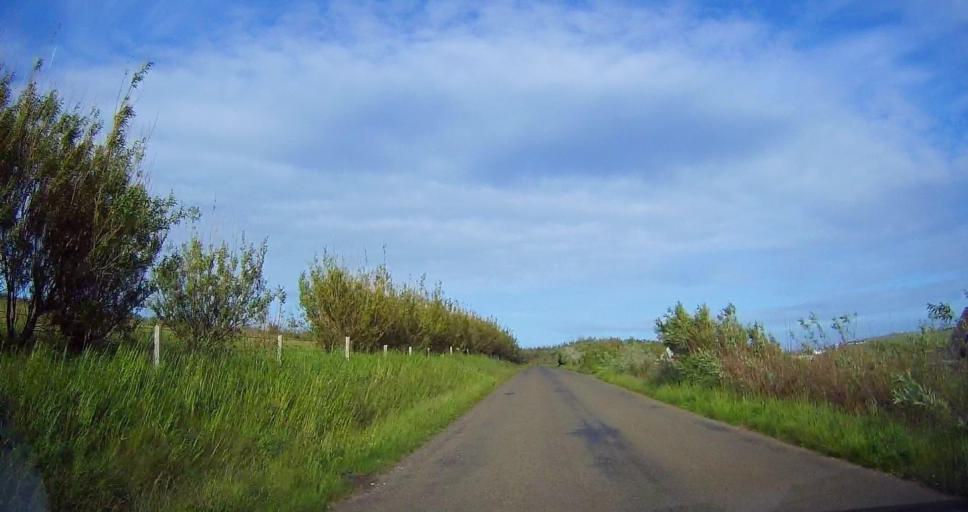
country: GB
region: Scotland
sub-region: Orkney Islands
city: Stromness
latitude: 58.8033
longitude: -3.2289
